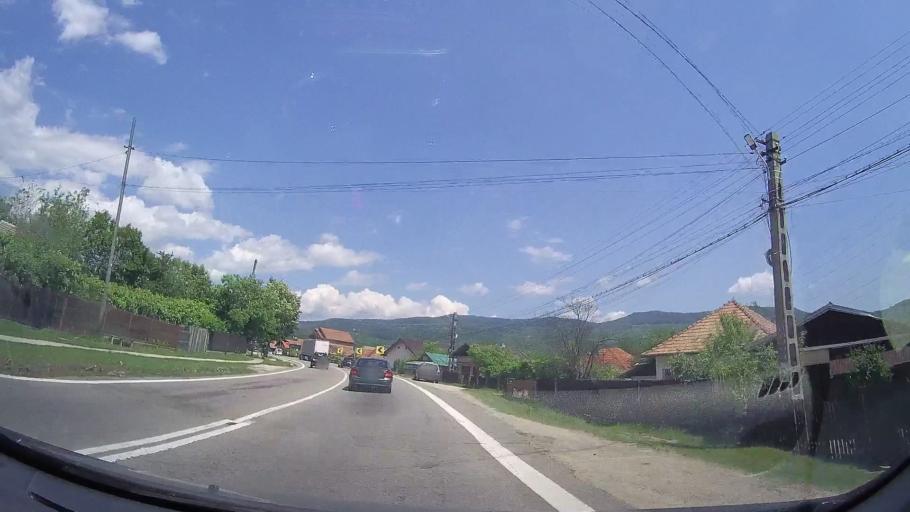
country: RO
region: Valcea
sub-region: Comuna Daesti
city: Daesti
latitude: 45.1917
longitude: 24.3737
